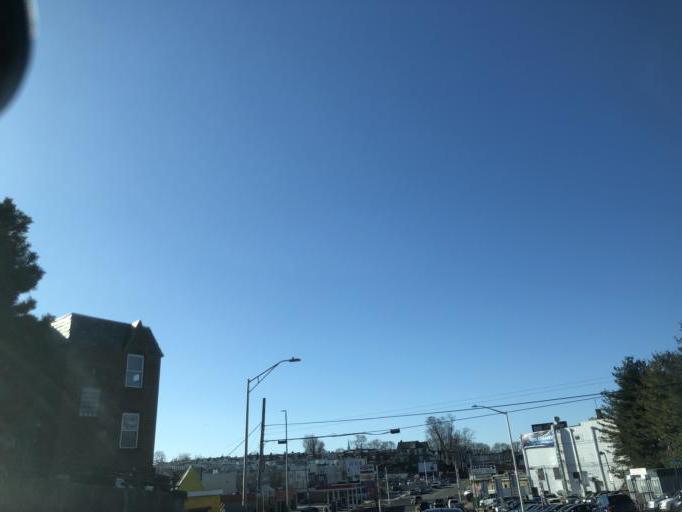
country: US
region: Pennsylvania
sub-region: Delaware County
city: East Lansdowne
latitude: 39.9547
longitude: -75.2569
